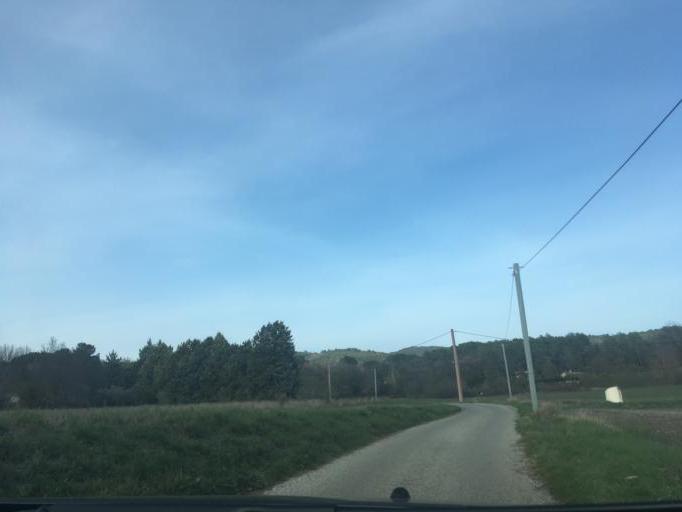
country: FR
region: Provence-Alpes-Cote d'Azur
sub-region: Departement du Var
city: Villecroze
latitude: 43.5640
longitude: 6.2834
